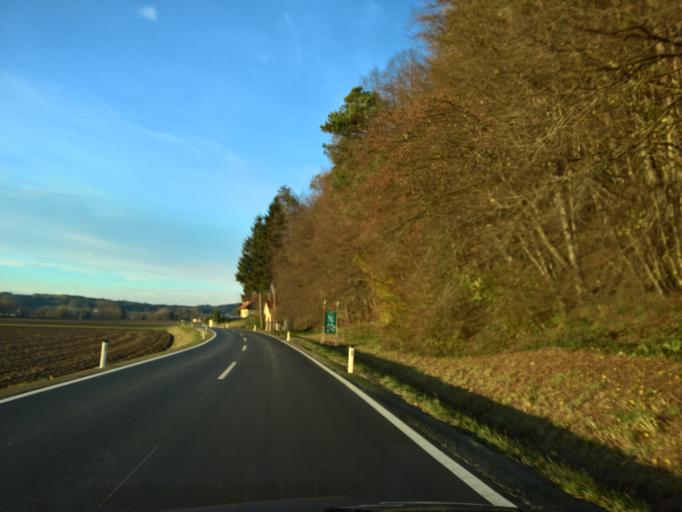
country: AT
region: Styria
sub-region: Politischer Bezirk Leibnitz
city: Arnfels
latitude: 46.6868
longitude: 15.3967
